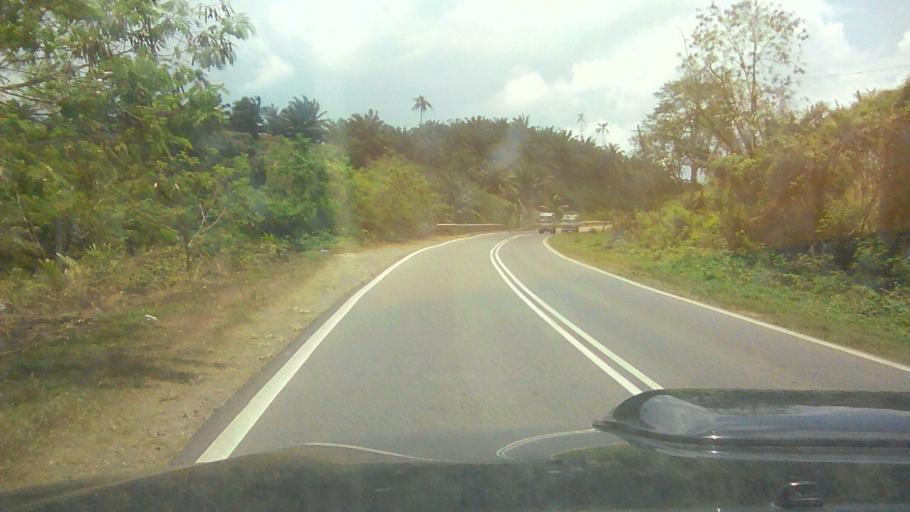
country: MY
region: Sabah
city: Lahad Datu
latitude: 5.0326
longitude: 118.4125
